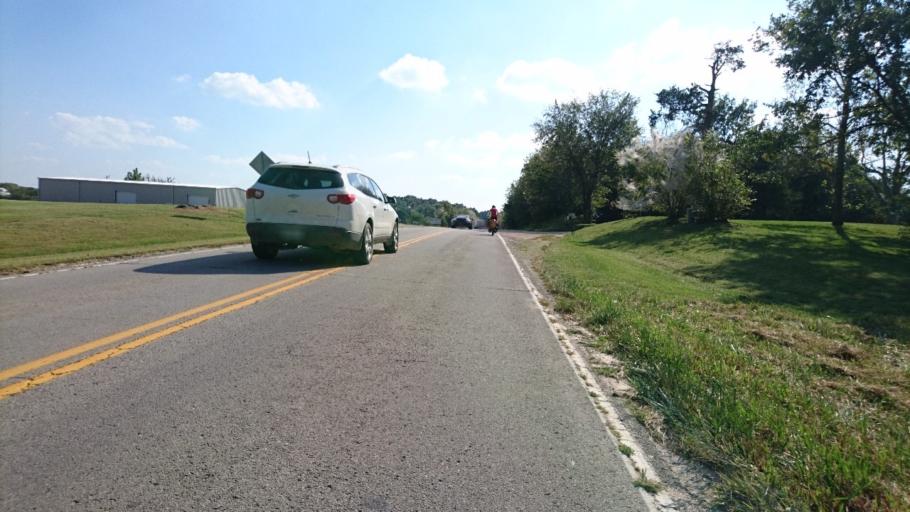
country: US
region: Missouri
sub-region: Laclede County
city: Lebanon
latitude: 37.6258
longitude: -92.6905
